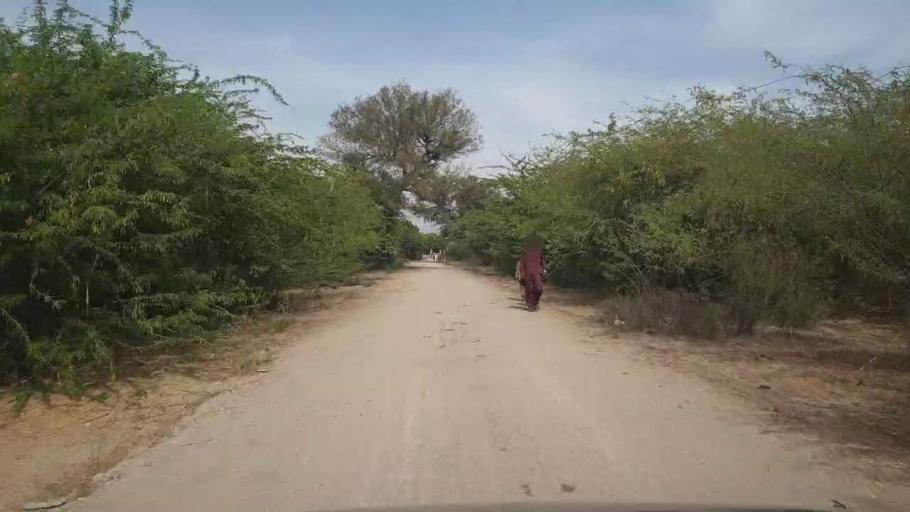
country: PK
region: Sindh
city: Umarkot
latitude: 25.2584
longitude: 69.7241
